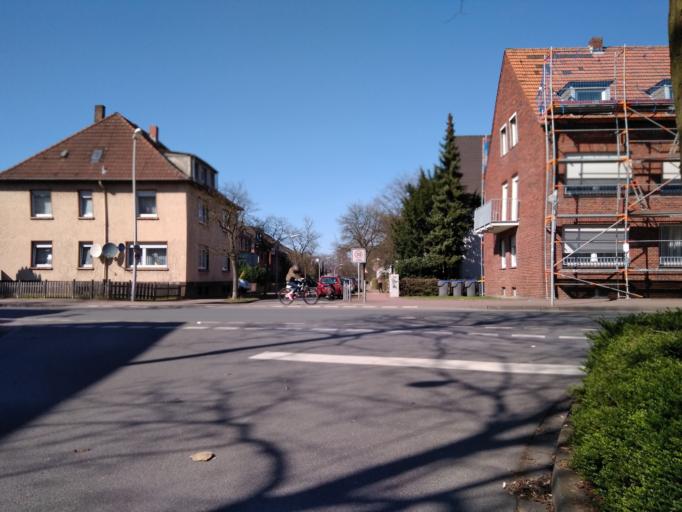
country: DE
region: North Rhine-Westphalia
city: Dorsten
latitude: 51.6608
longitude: 6.9595
